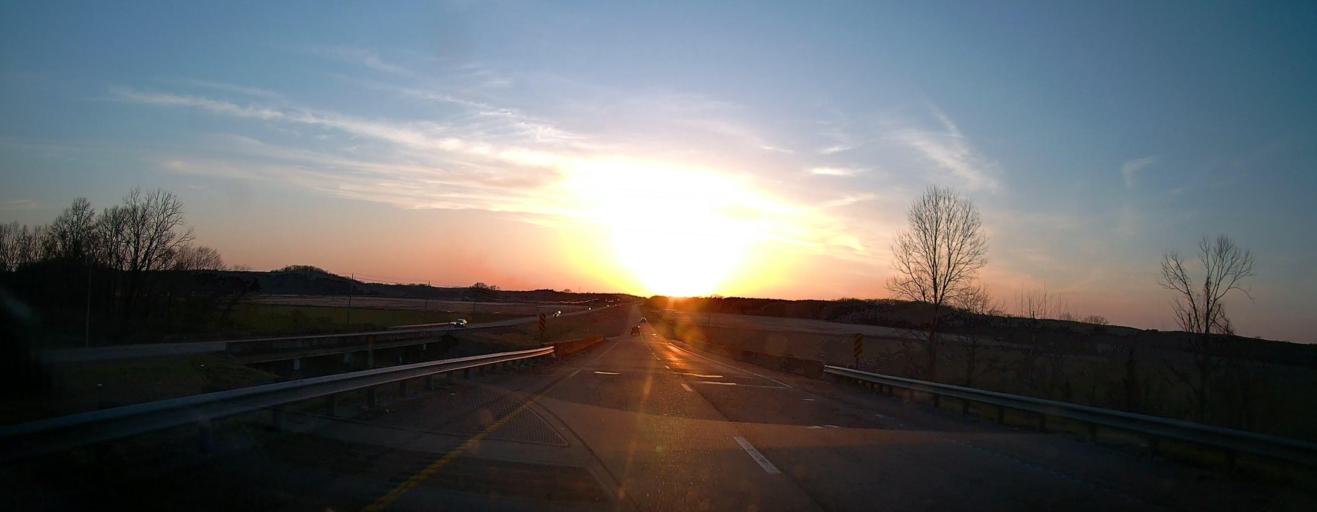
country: US
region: Mississippi
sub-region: Alcorn County
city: Corinth
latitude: 34.9326
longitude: -88.6515
